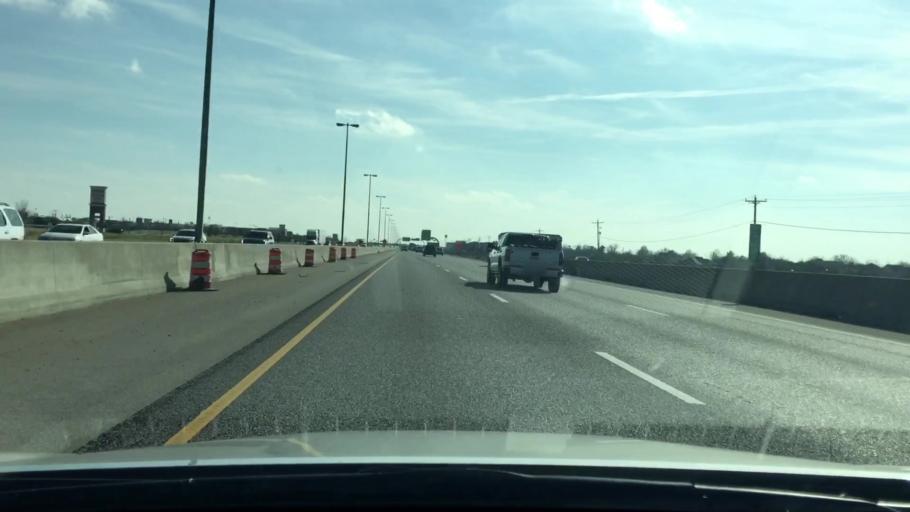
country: US
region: Oklahoma
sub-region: Cleveland County
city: Norman
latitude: 35.2452
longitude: -97.4856
